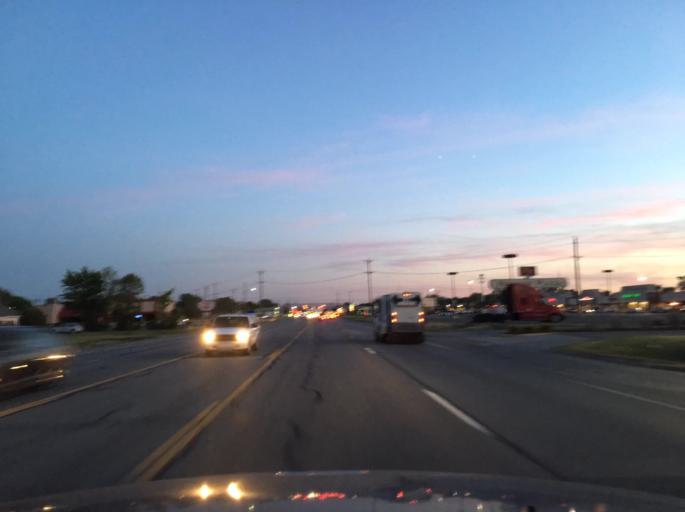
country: US
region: Michigan
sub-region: Macomb County
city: Clinton
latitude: 42.5722
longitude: -82.9101
